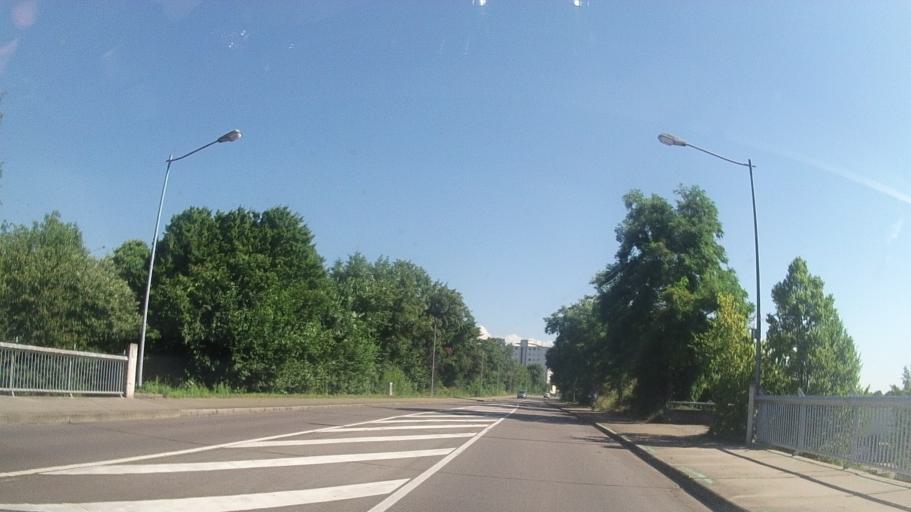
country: DE
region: Baden-Wuerttemberg
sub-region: Freiburg Region
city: Offenburg
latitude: 48.4848
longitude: 7.9386
